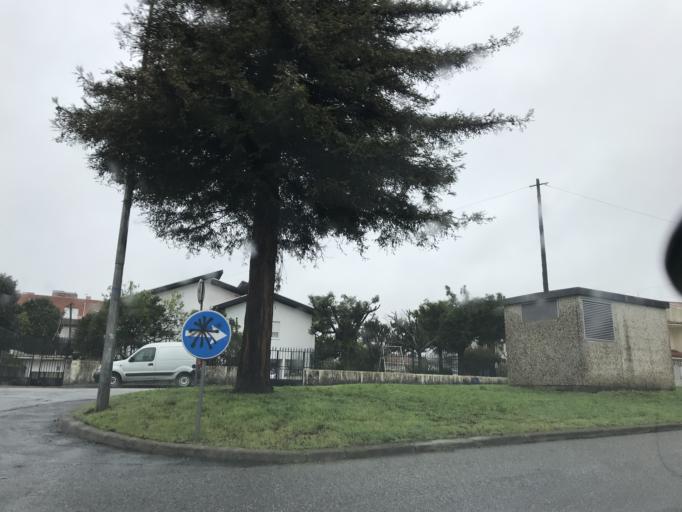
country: PT
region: Braga
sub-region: Vila Nova de Famalicao
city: Vila Nova de Famalicao
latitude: 41.4119
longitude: -8.5139
